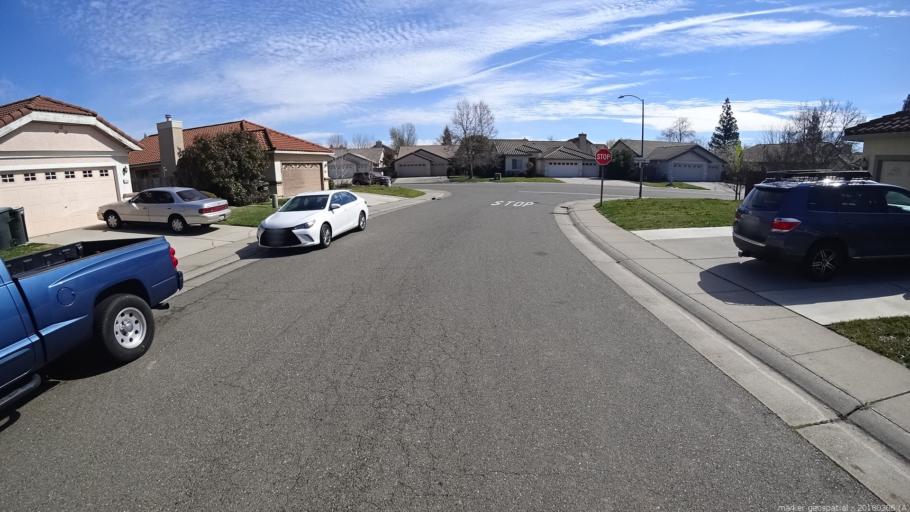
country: US
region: California
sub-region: Sacramento County
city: Vineyard
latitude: 38.4609
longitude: -121.3486
